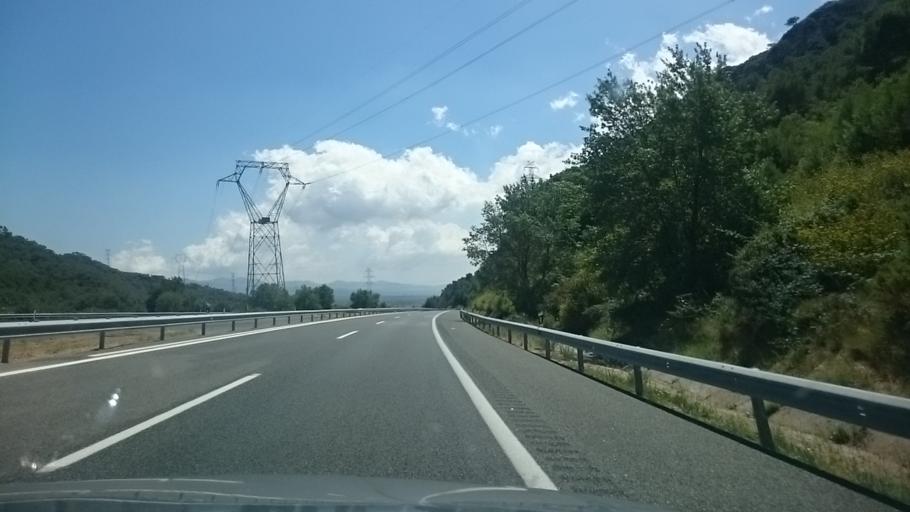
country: ES
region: Catalonia
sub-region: Provincia de Tarragona
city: Cabra del Camp
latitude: 41.3922
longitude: 1.2764
